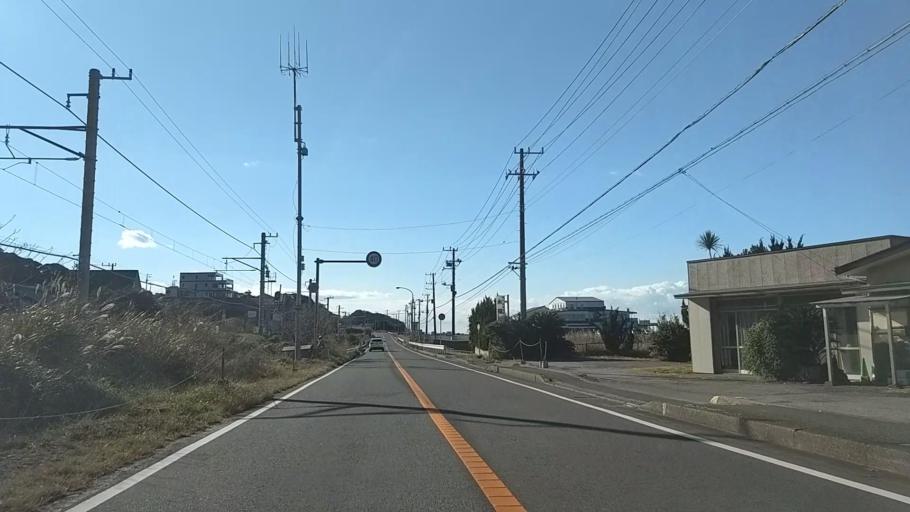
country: JP
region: Chiba
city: Futtsu
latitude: 35.1872
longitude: 139.8194
